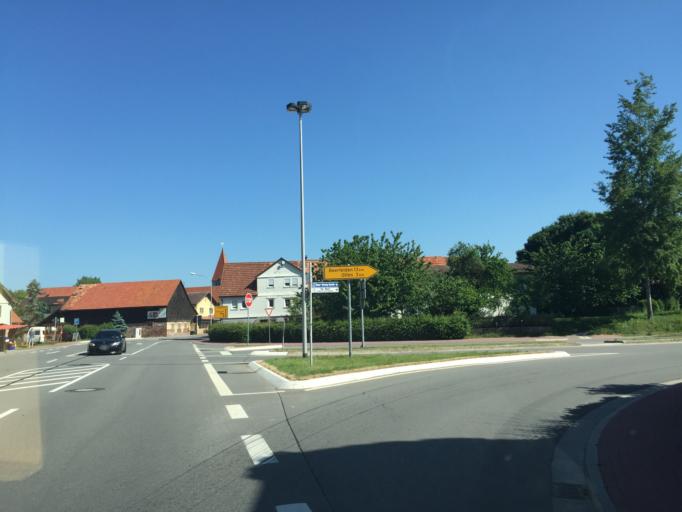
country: DE
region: Hesse
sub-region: Regierungsbezirk Darmstadt
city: Wald-Michelbach
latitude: 49.5959
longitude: 8.8553
